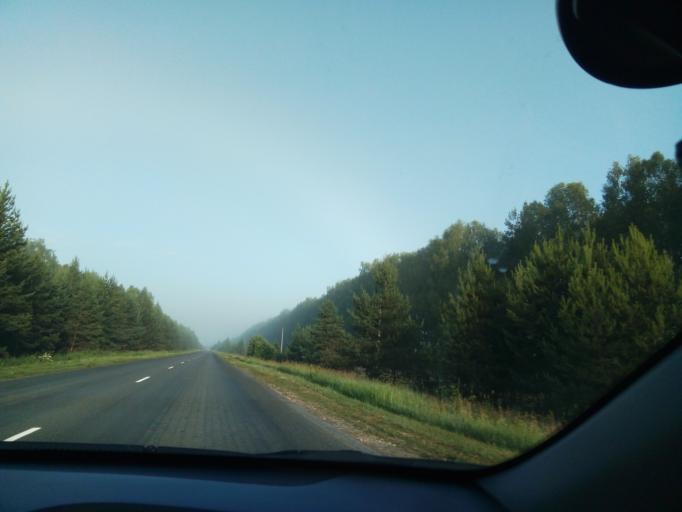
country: RU
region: Nizjnij Novgorod
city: Voznesenskoye
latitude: 54.8620
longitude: 42.9344
